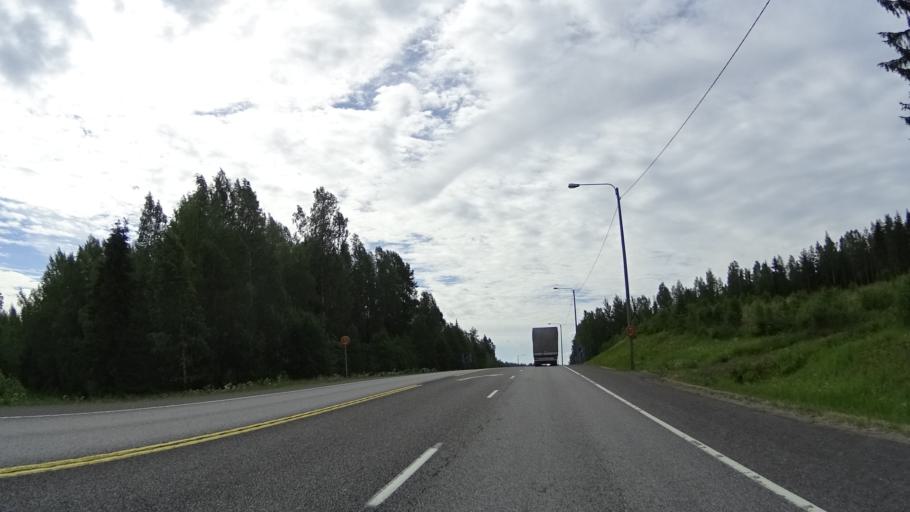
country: FI
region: Uusimaa
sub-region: Helsinki
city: Karkkila
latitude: 60.5105
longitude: 24.2613
